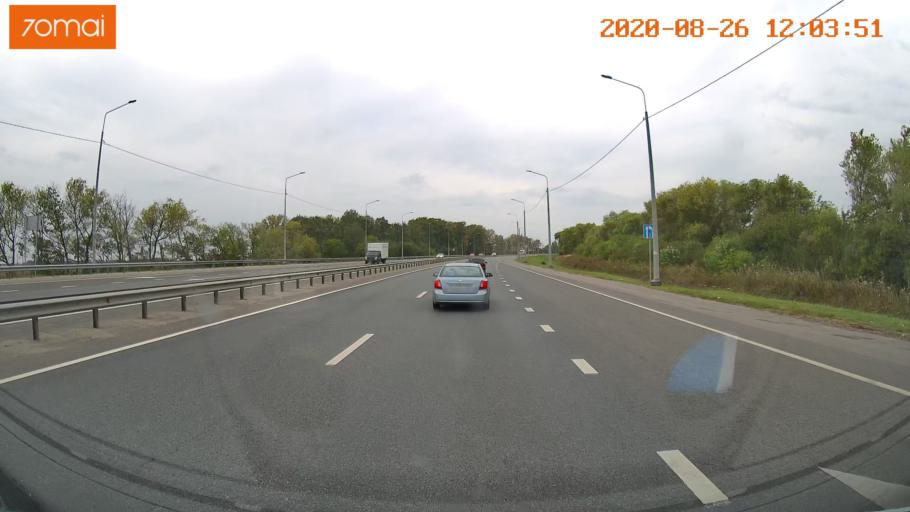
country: RU
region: Rjazan
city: Kiritsy
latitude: 54.3038
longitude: 40.1984
